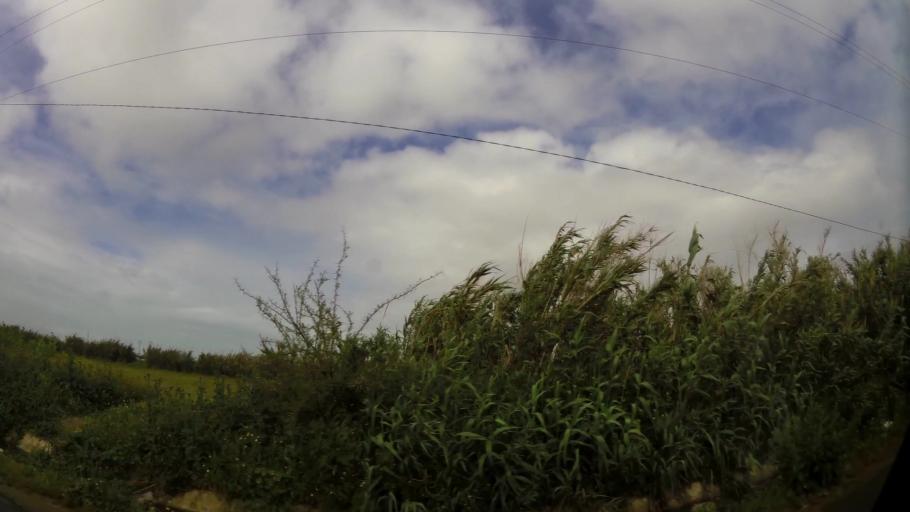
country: MA
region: Grand Casablanca
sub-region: Mohammedia
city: Mohammedia
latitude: 33.6483
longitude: -7.4554
